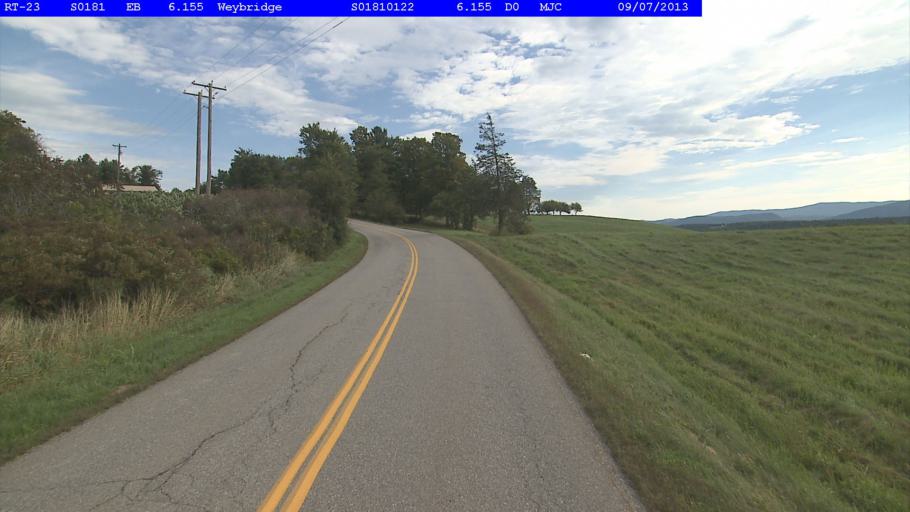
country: US
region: Vermont
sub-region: Addison County
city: Vergennes
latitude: 44.0783
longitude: -73.2515
